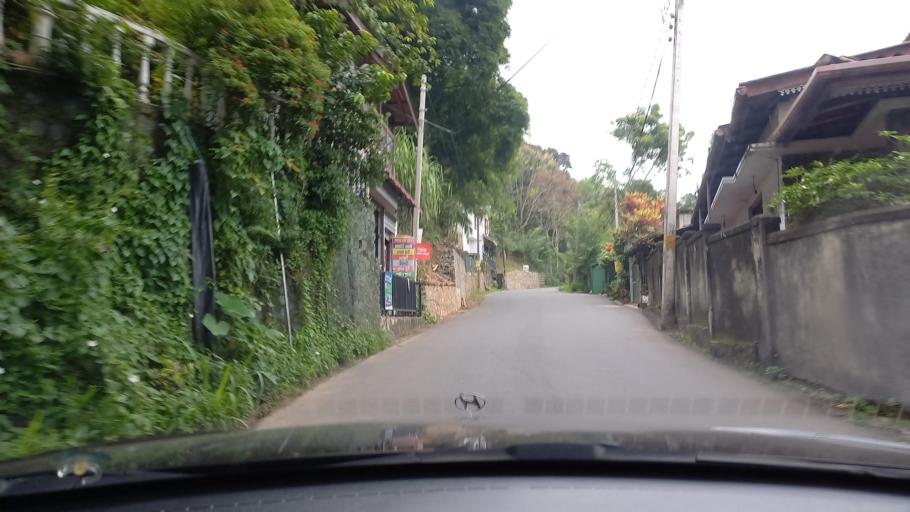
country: LK
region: Central
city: Kandy
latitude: 7.2378
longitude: 80.6017
